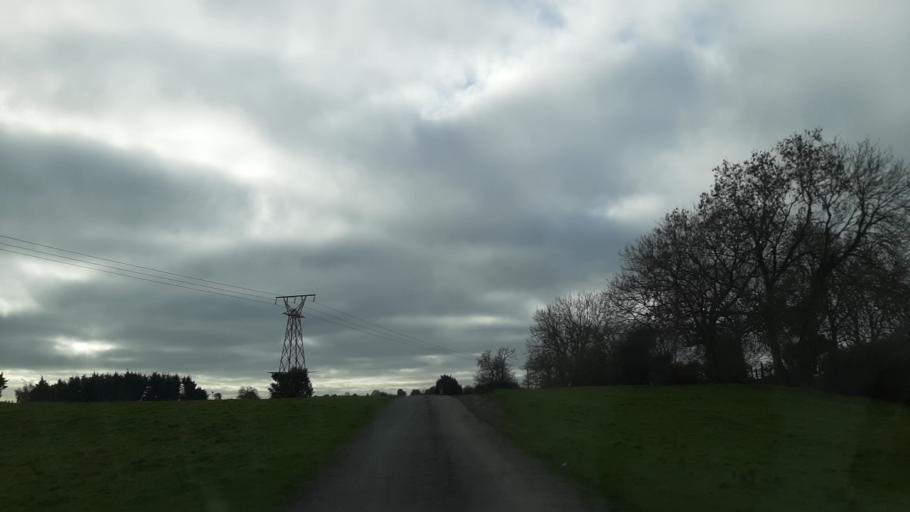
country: IE
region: Leinster
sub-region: Kildare
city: Kildare
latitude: 53.1741
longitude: -6.8987
